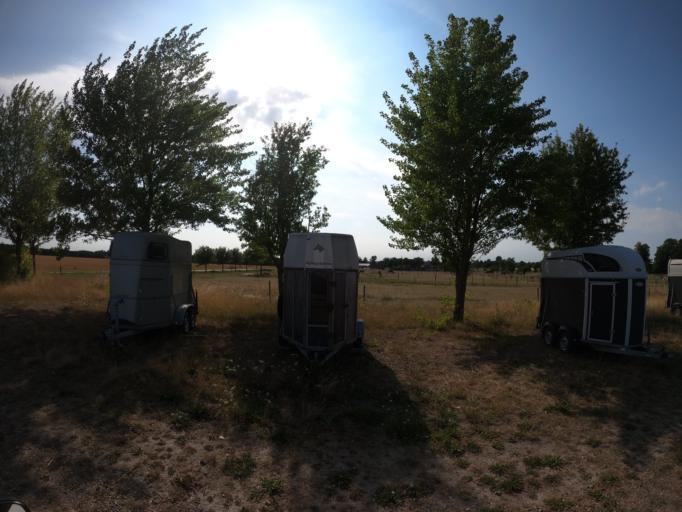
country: SE
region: Skane
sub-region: Lunds Kommun
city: Lund
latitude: 55.7395
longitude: 13.1861
